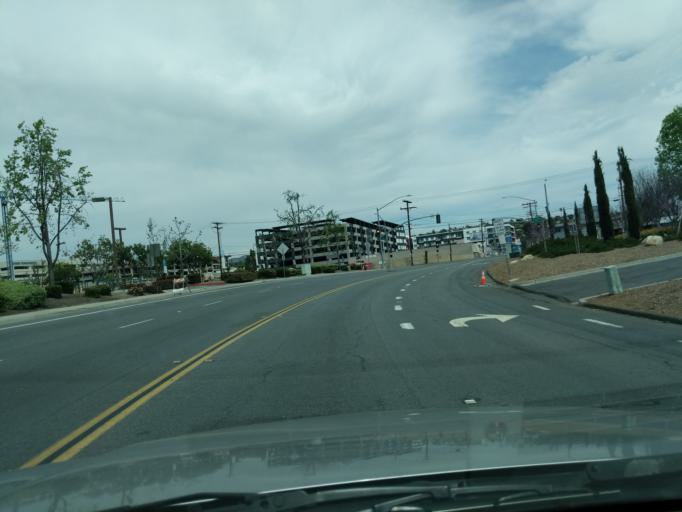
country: US
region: California
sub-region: San Diego County
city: La Mesa
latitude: 32.7849
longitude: -117.1025
